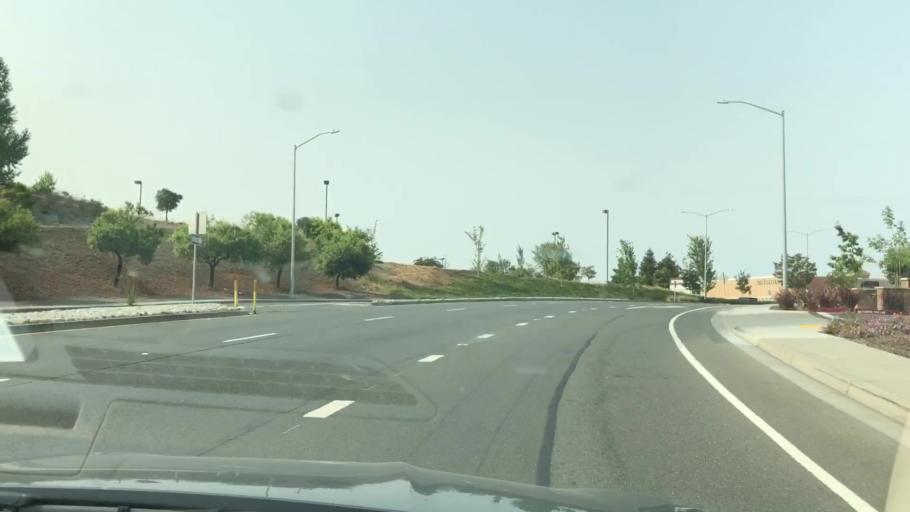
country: US
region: California
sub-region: Solano County
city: Vallejo
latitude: 38.1364
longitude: -122.2138
